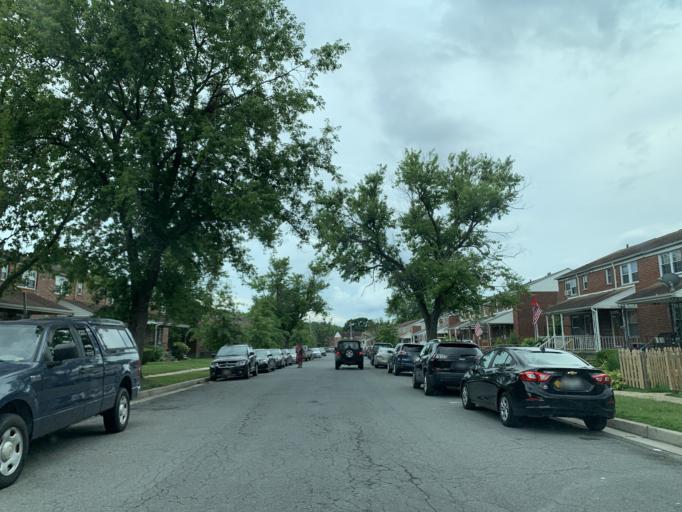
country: US
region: Maryland
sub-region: Baltimore County
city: Essex
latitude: 39.2967
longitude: -76.4509
